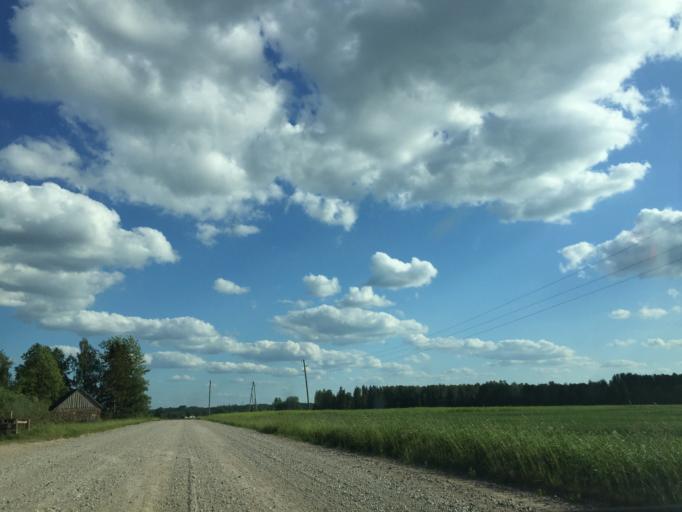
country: LV
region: Kandava
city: Kandava
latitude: 56.9103
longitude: 22.7921
